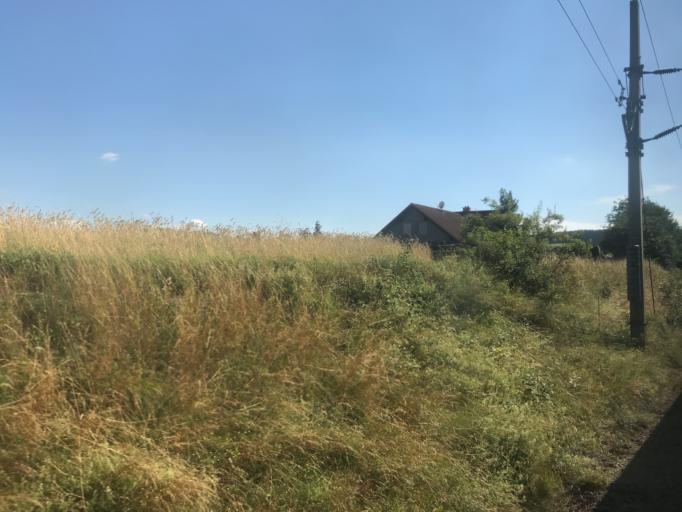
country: AT
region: Upper Austria
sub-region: Politischer Bezirk Urfahr-Umgebung
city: Reichenthal
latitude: 48.5556
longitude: 14.4402
